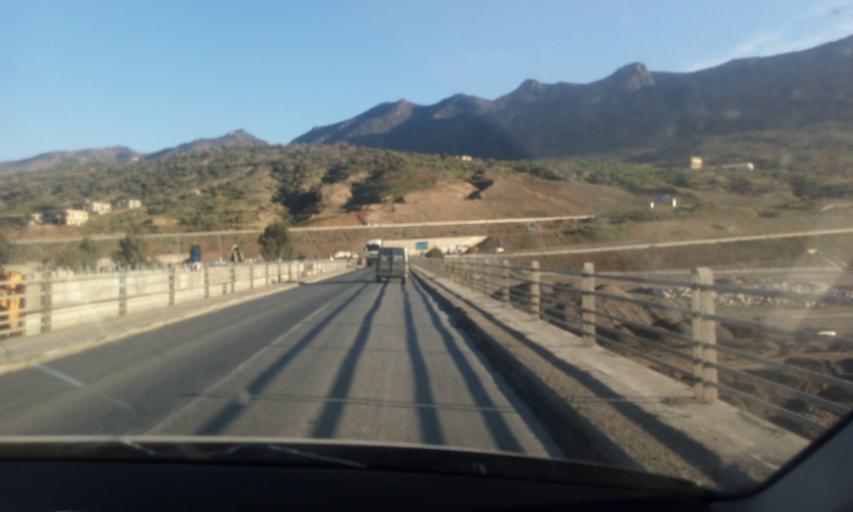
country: DZ
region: Bejaia
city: Akbou
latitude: 36.4813
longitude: 4.5920
